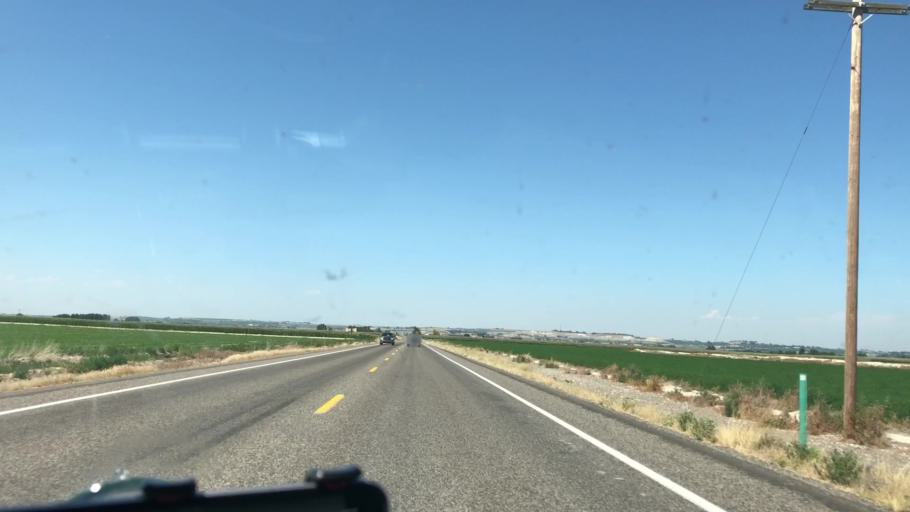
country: US
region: Idaho
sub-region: Owyhee County
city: Marsing
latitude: 43.5315
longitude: -116.8515
